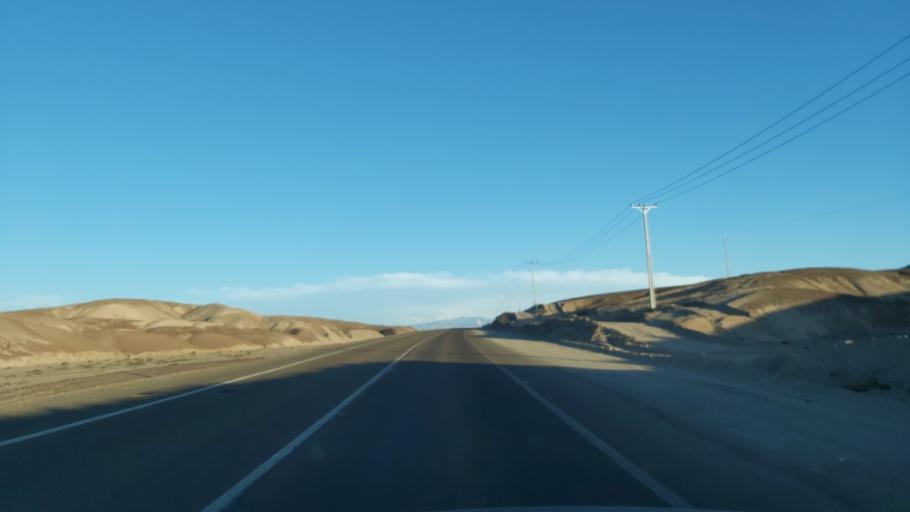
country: CL
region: Atacama
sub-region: Provincia de Chanaral
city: Diego de Almagro
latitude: -26.4188
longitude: -70.0267
